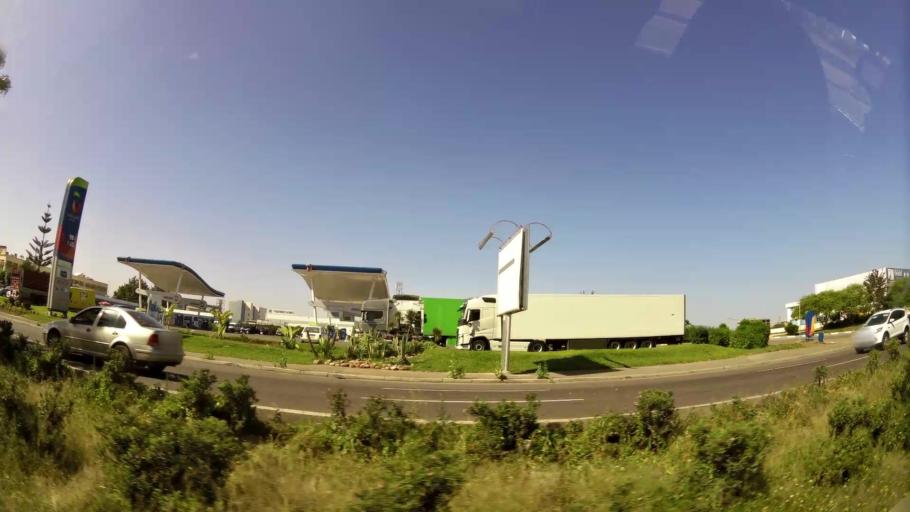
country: MA
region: Oued ed Dahab-Lagouira
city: Dakhla
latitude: 30.3938
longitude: -9.5188
